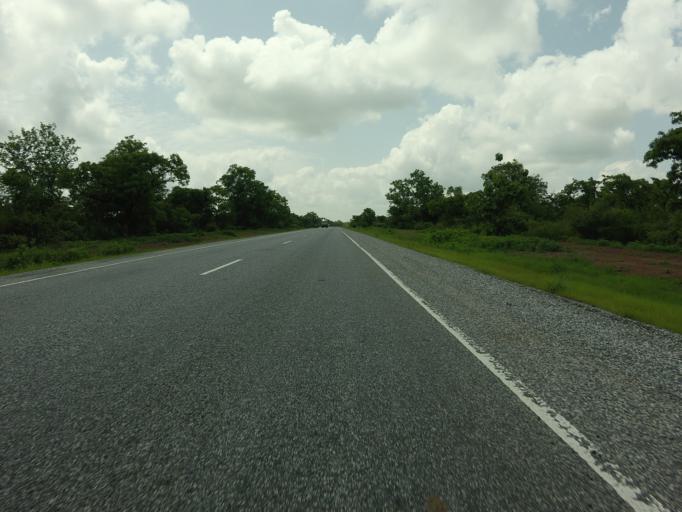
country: GH
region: Northern
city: Tamale
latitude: 9.1495
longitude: -1.3837
